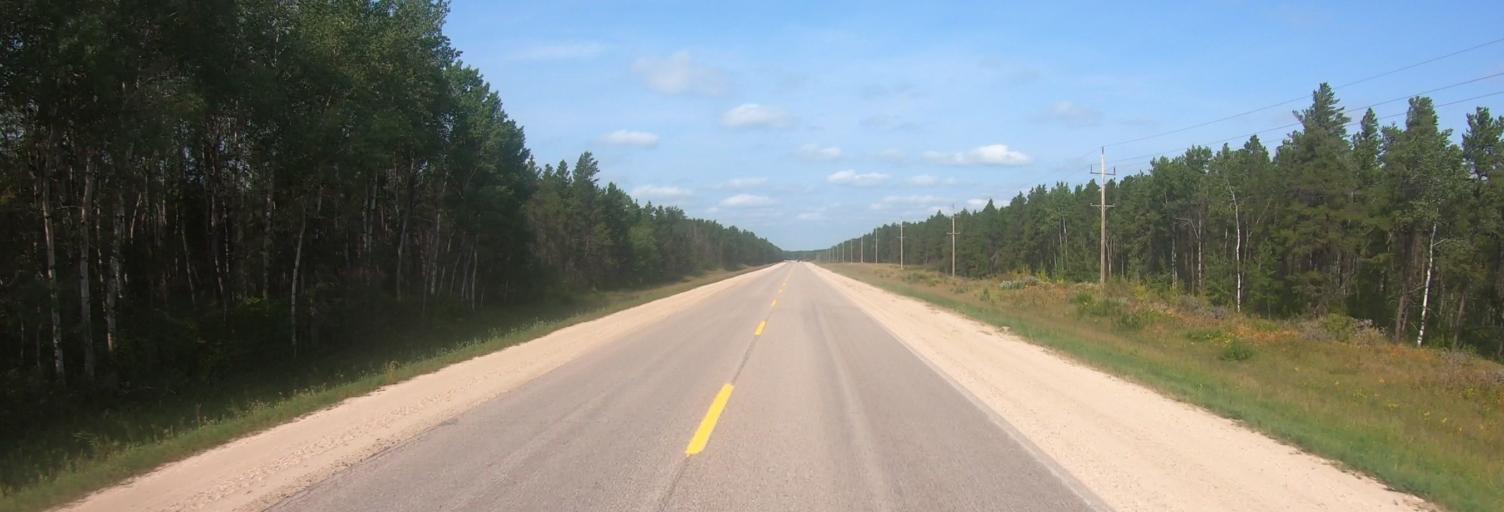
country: CA
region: Manitoba
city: La Broquerie
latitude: 49.1786
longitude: -96.1880
